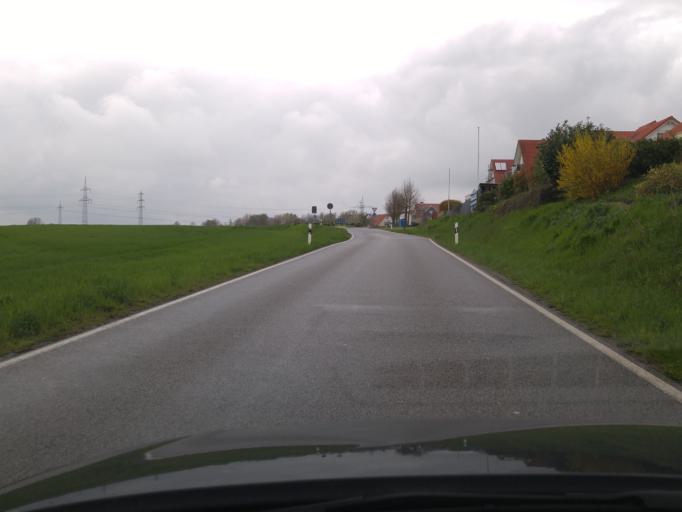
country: DE
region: Baden-Wuerttemberg
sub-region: Regierungsbezirk Stuttgart
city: Bad Rappenau
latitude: 49.2483
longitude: 9.1254
